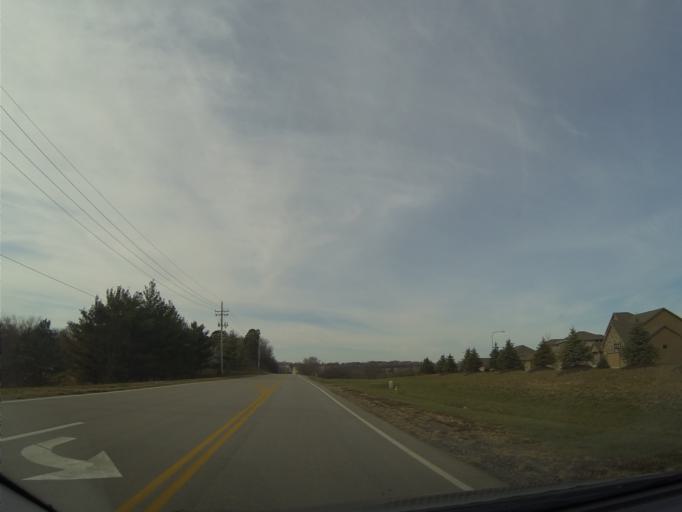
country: US
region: Nebraska
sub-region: Douglas County
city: Elkhorn
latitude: 41.2776
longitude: -96.1923
